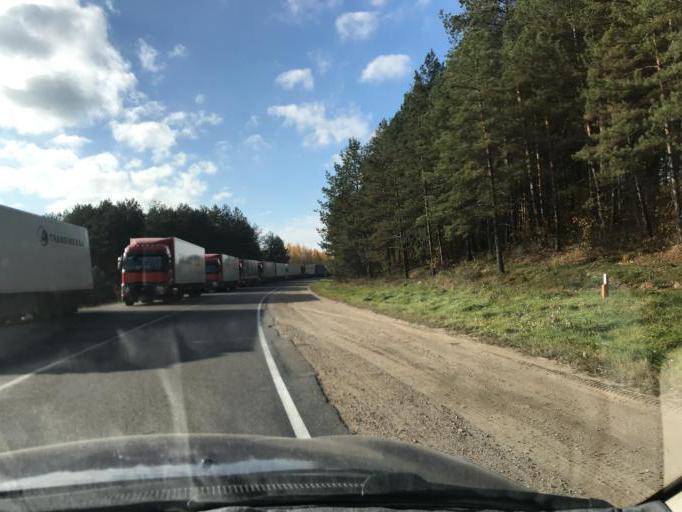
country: LT
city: Salcininkai
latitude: 54.2651
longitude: 25.3689
